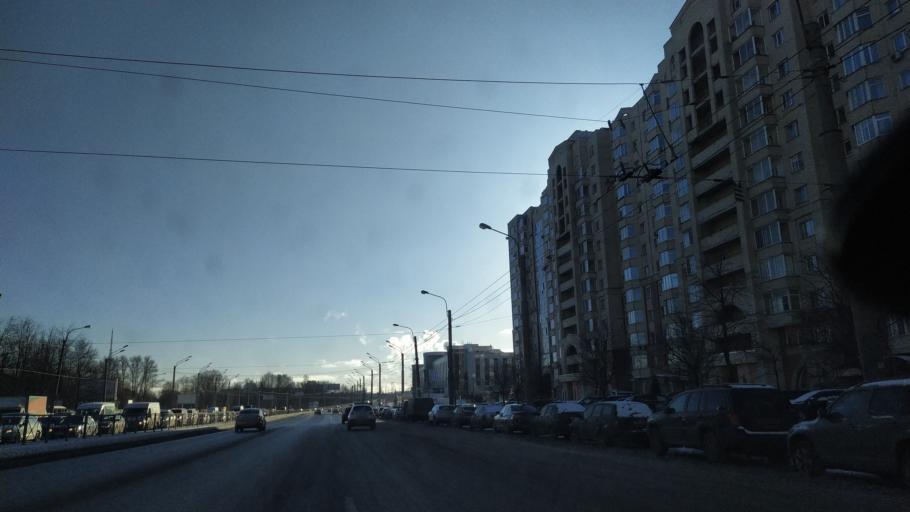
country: RU
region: Leningrad
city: Chernaya Rechka
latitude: 59.9991
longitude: 30.2990
